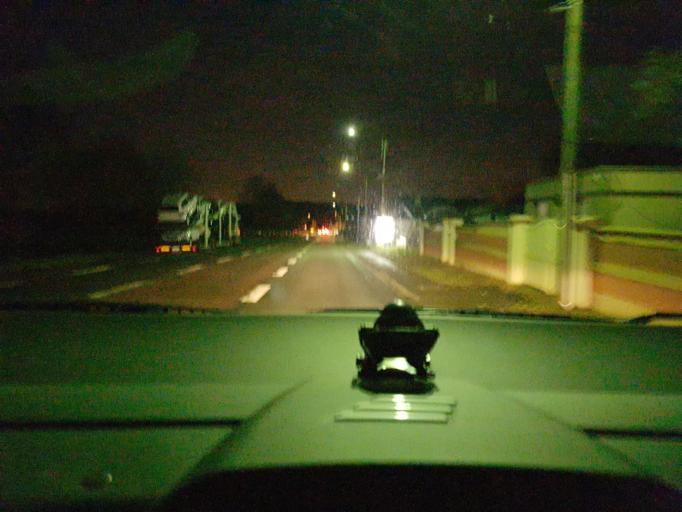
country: FR
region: Nord-Pas-de-Calais
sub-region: Departement du Pas-de-Calais
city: Souchez
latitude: 50.3827
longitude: 2.7431
